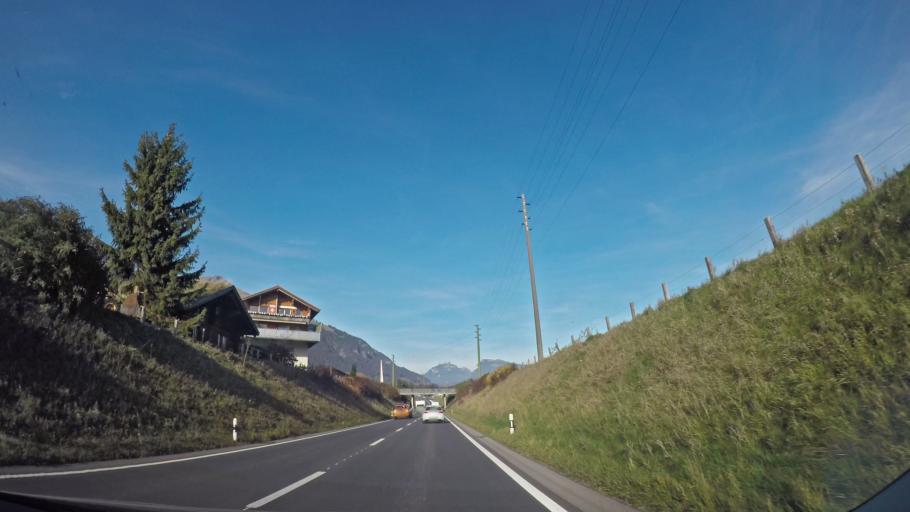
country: CH
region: Bern
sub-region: Frutigen-Niedersimmental District
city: Frutigen
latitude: 46.5903
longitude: 7.6552
